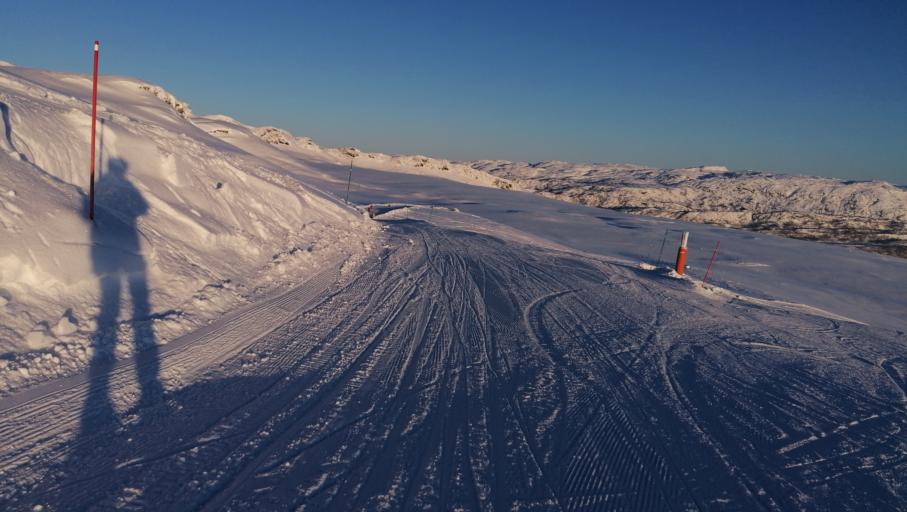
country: NO
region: Aust-Agder
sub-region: Bykle
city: Hovden
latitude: 59.5817
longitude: 7.3320
